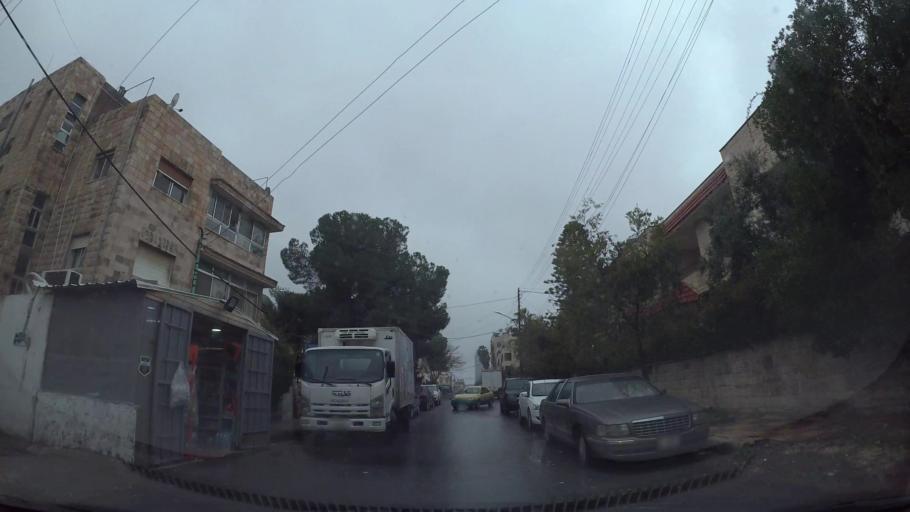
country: JO
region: Amman
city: Amman
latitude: 31.9714
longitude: 35.9179
